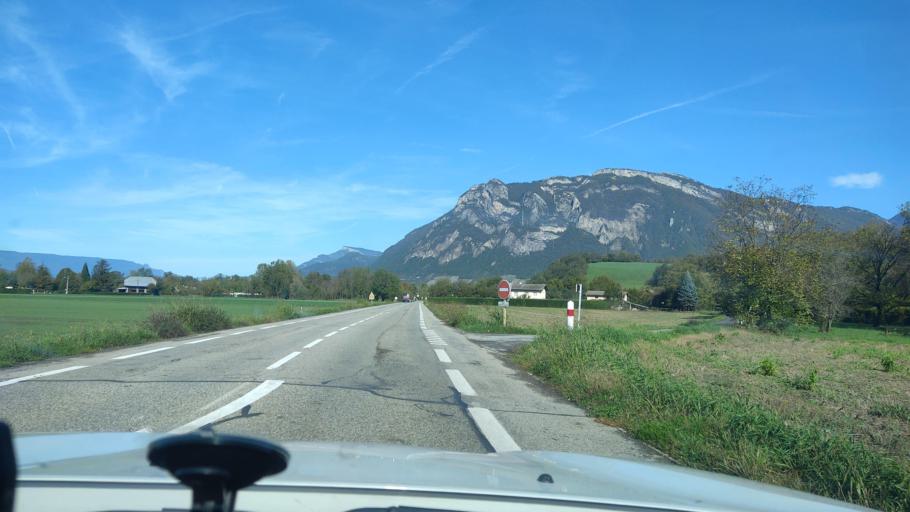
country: FR
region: Rhone-Alpes
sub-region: Departement de la Savoie
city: Montmelian
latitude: 45.4729
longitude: 6.0428
